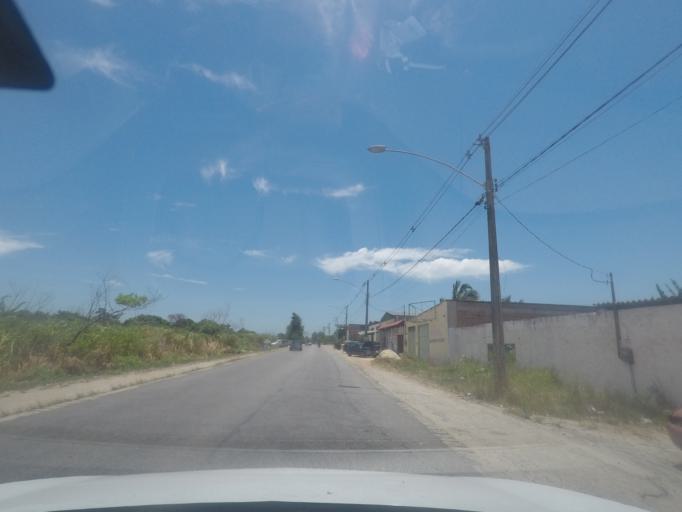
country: BR
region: Rio de Janeiro
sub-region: Itaguai
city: Itaguai
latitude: -22.9015
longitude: -43.6907
